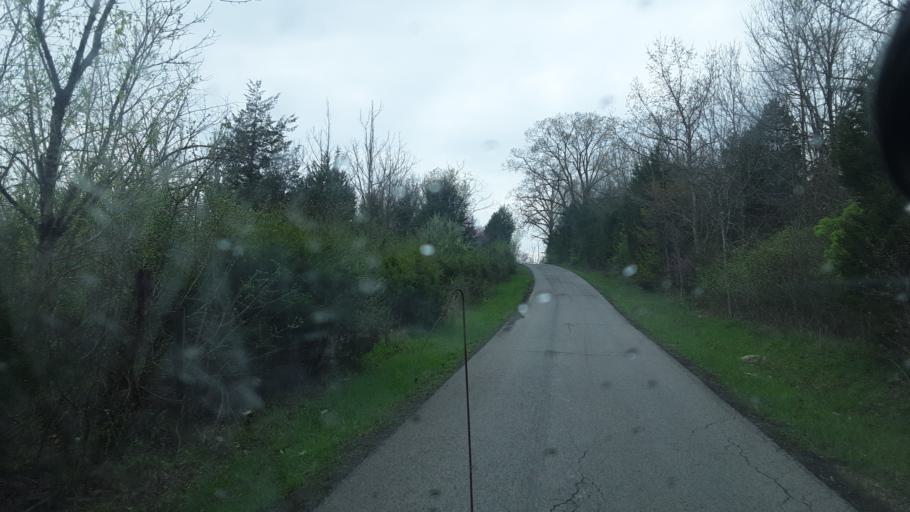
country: US
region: Kentucky
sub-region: Owen County
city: Owenton
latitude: 38.6761
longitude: -84.7995
